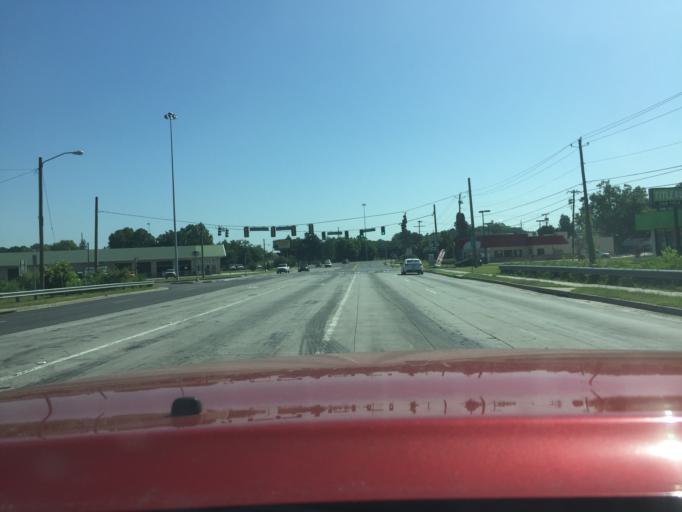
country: US
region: Georgia
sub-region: Chatham County
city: Garden City
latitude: 32.0961
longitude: -81.1438
